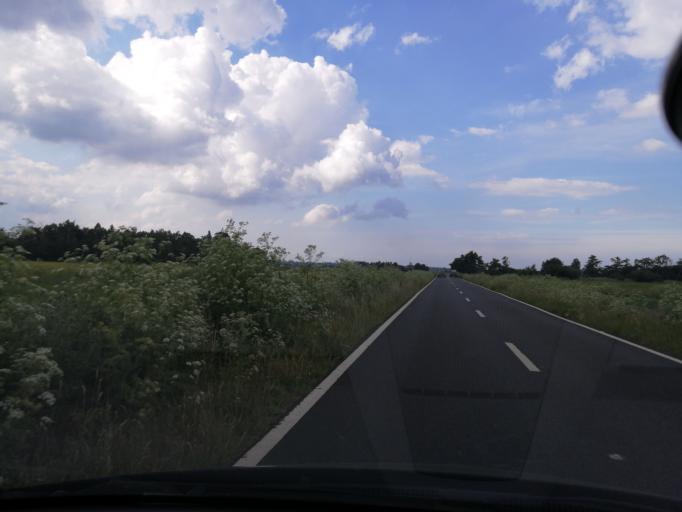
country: GB
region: England
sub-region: Cambridgeshire
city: Yaxley
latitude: 52.4862
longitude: -0.2431
